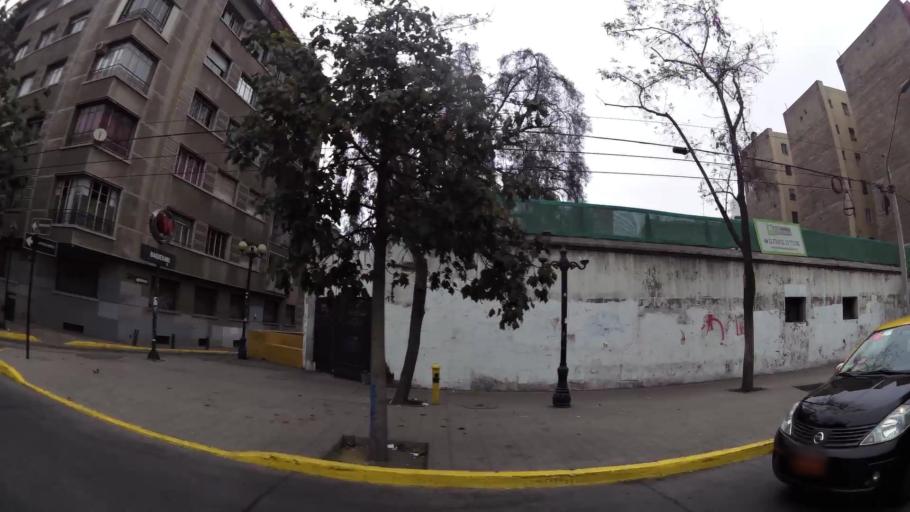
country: CL
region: Santiago Metropolitan
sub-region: Provincia de Santiago
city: Santiago
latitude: -33.4382
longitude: -70.6333
